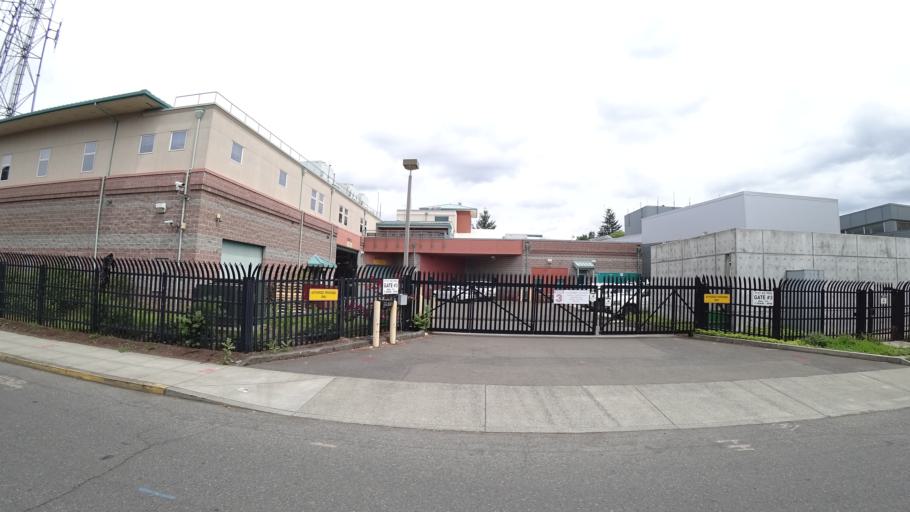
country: US
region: Oregon
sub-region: Multnomah County
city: Lents
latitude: 45.4952
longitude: -122.5617
